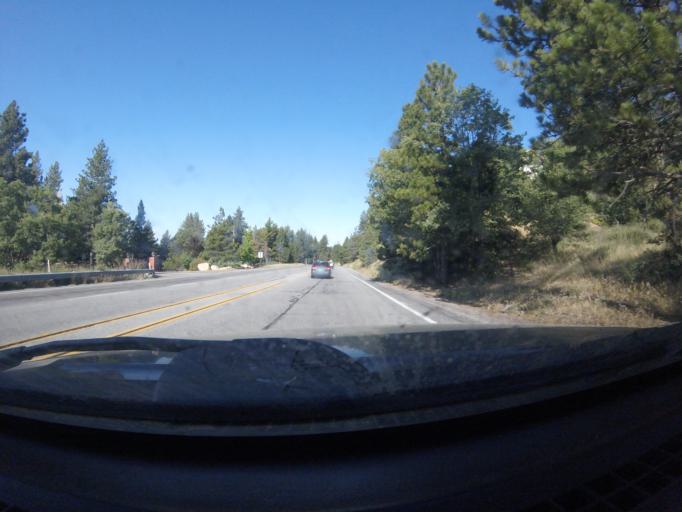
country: US
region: California
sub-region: San Bernardino County
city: Running Springs
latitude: 34.2044
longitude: -117.1446
